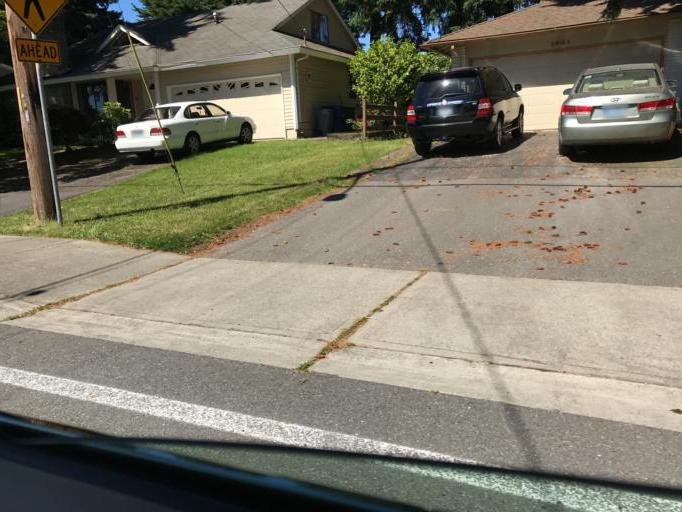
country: US
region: Washington
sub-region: King County
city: Sammamish
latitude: 47.6271
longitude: -122.1211
